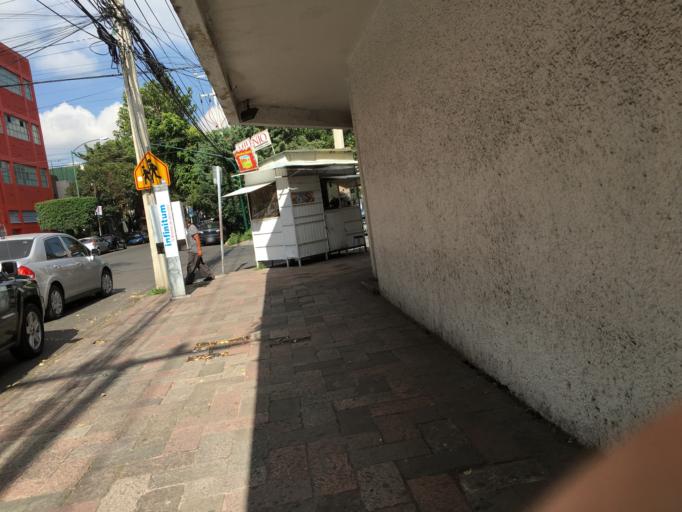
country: MX
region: Mexico City
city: Colonia del Valle
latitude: 19.3749
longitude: -99.1636
